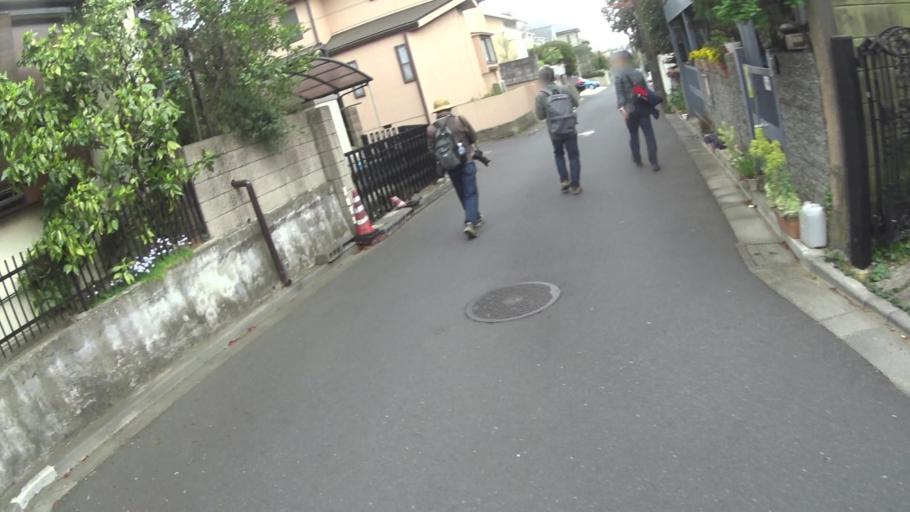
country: JP
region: Tokyo
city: Chofugaoka
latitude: 35.6725
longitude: 139.5393
